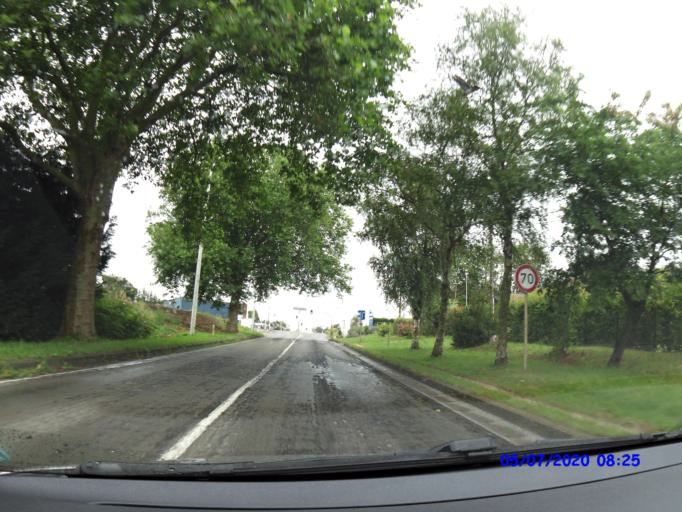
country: BE
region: Wallonia
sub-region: Province du Brabant Wallon
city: Genappe
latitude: 50.5705
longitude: 4.4556
